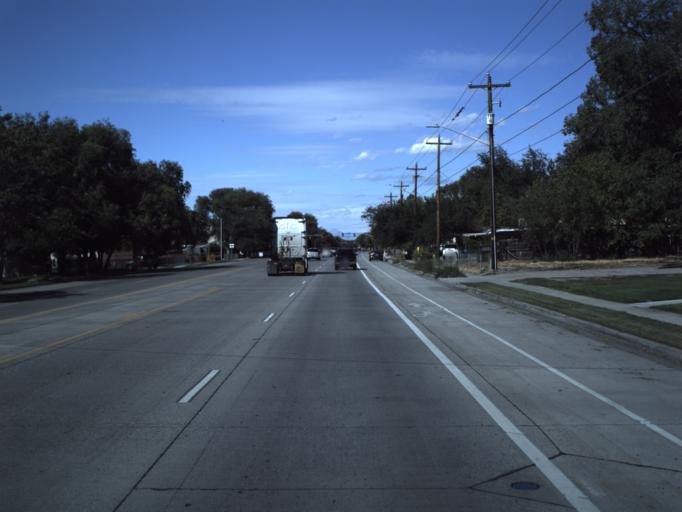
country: US
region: Utah
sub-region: Salt Lake County
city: Salt Lake City
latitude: 40.7771
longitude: -111.9393
